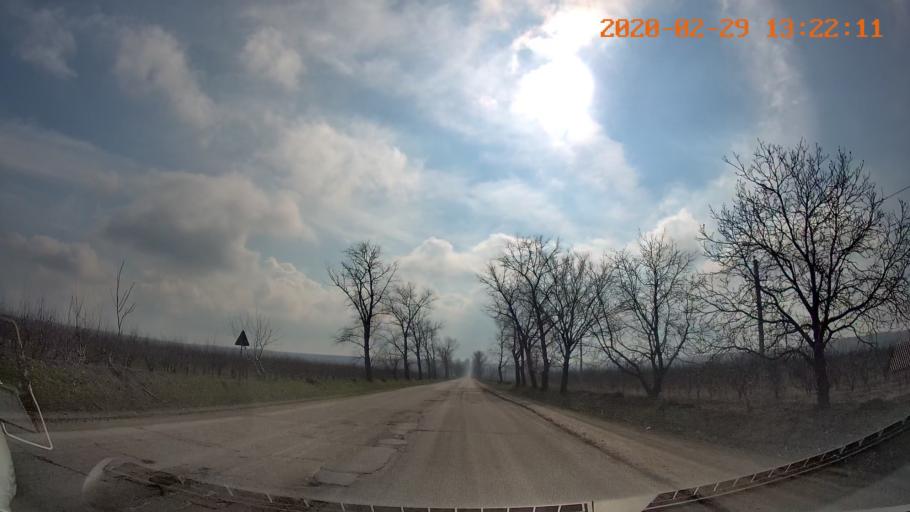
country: MD
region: Telenesti
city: Camenca
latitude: 47.9632
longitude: 28.6284
